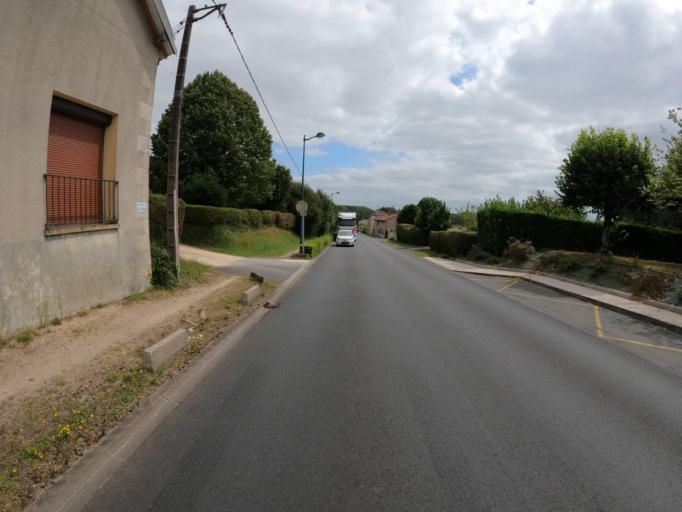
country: FR
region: Poitou-Charentes
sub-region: Departement de la Vienne
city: Savigne
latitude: 46.1598
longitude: 0.3190
